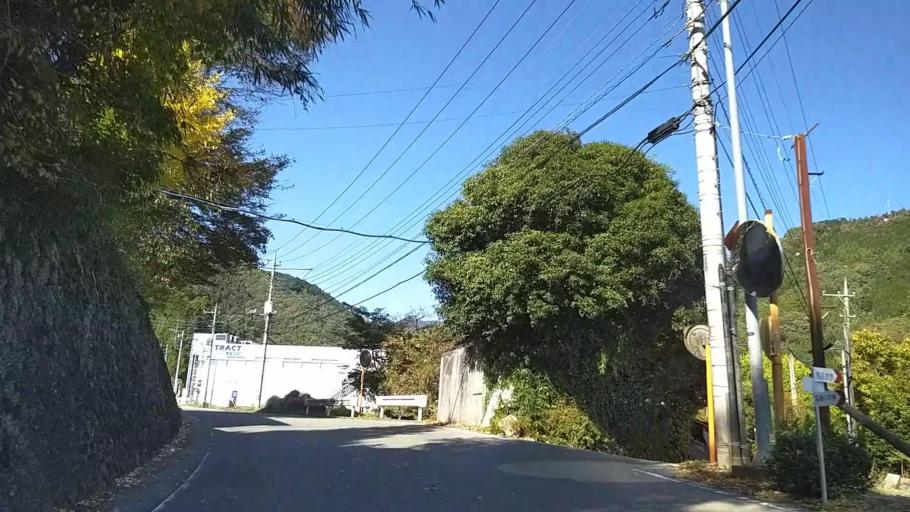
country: JP
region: Yamanashi
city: Uenohara
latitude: 35.6520
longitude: 139.0973
